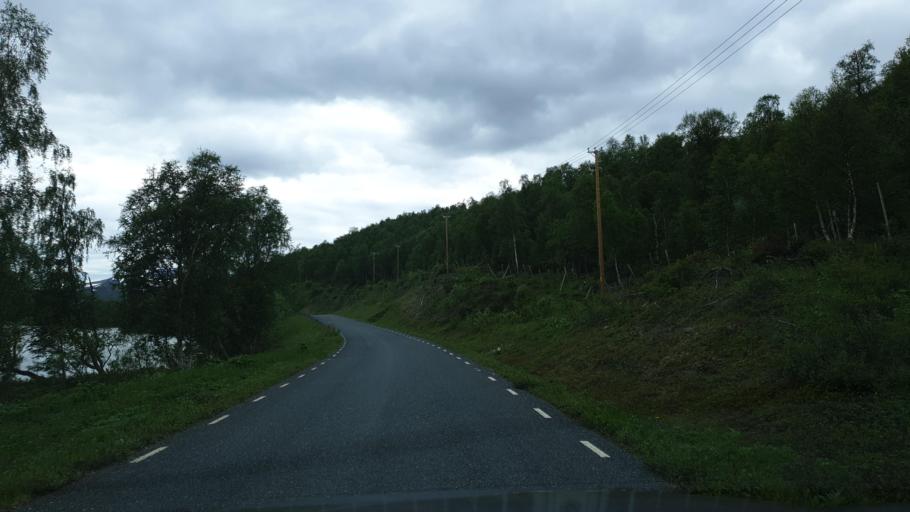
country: NO
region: Nordland
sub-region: Hattfjelldal
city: Hattfjelldal
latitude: 65.4186
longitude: 14.7658
